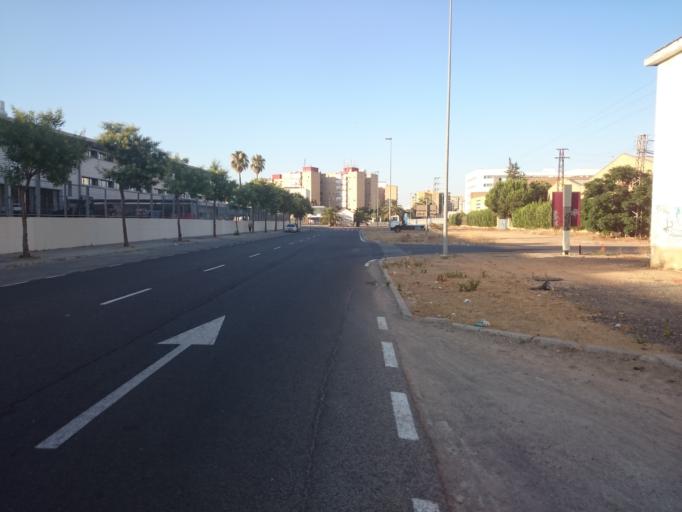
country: ES
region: Andalusia
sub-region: Provincia de Sevilla
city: Sevilla
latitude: 37.3886
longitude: -5.9499
